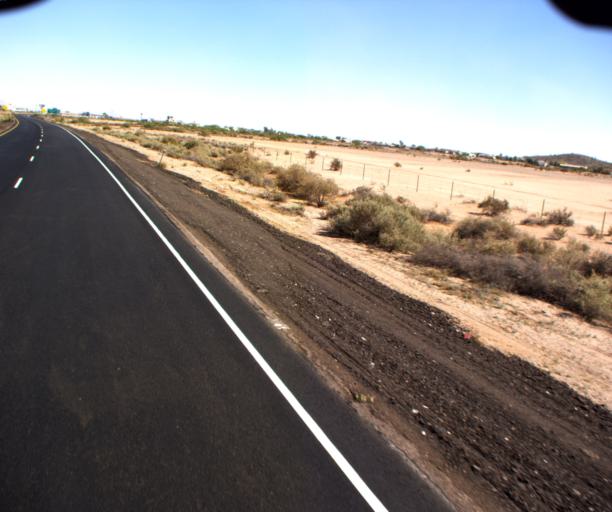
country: US
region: Arizona
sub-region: Pinal County
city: Arizona City
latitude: 32.8195
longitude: -111.6879
